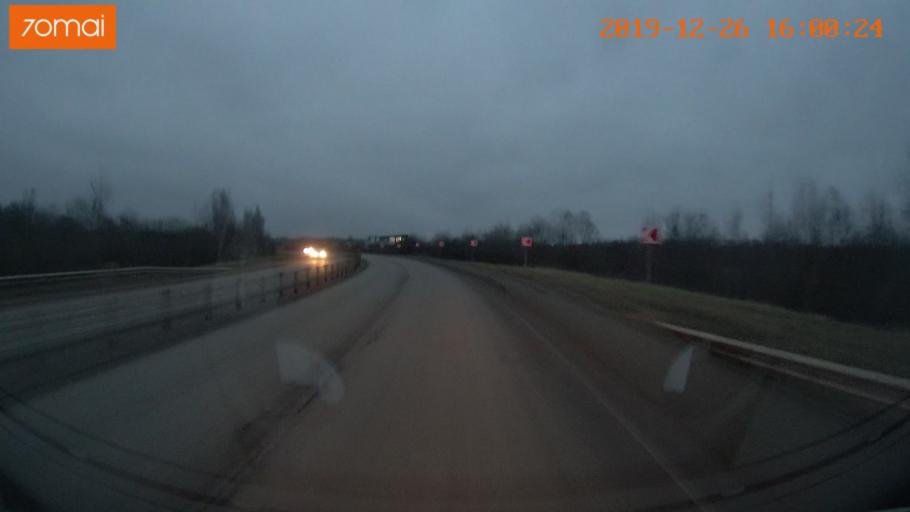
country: RU
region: Jaroslavl
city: Rybinsk
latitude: 58.0249
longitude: 38.8027
